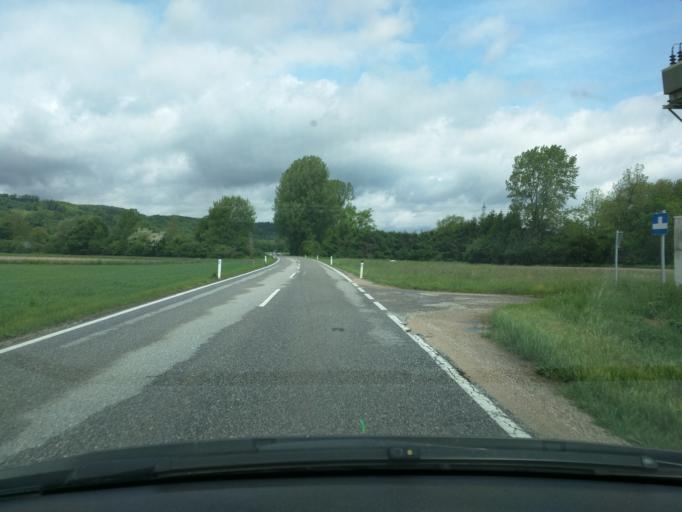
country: AT
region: Lower Austria
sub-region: Politischer Bezirk Melk
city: Blindenmarkt
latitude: 48.1212
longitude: 15.0136
